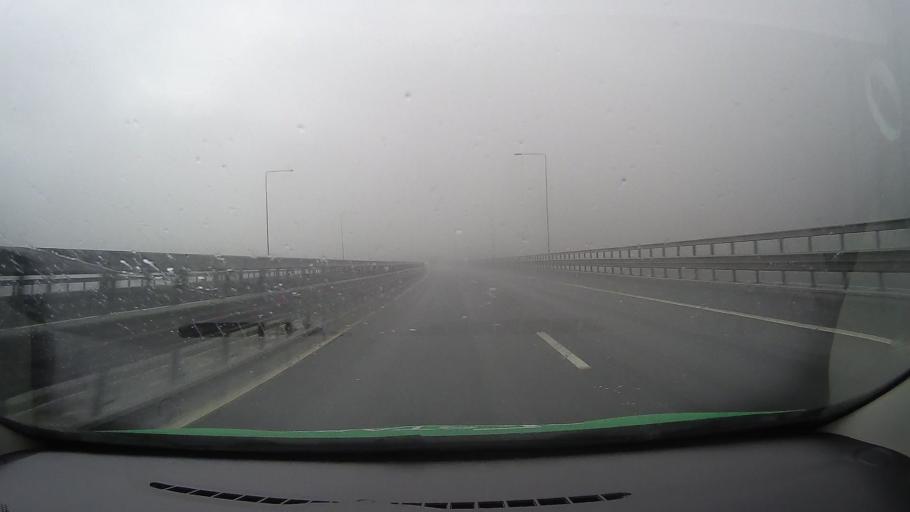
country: RO
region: Sibiu
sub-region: Comuna Tilisca
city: Tilisca
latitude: 45.8252
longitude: 23.8658
